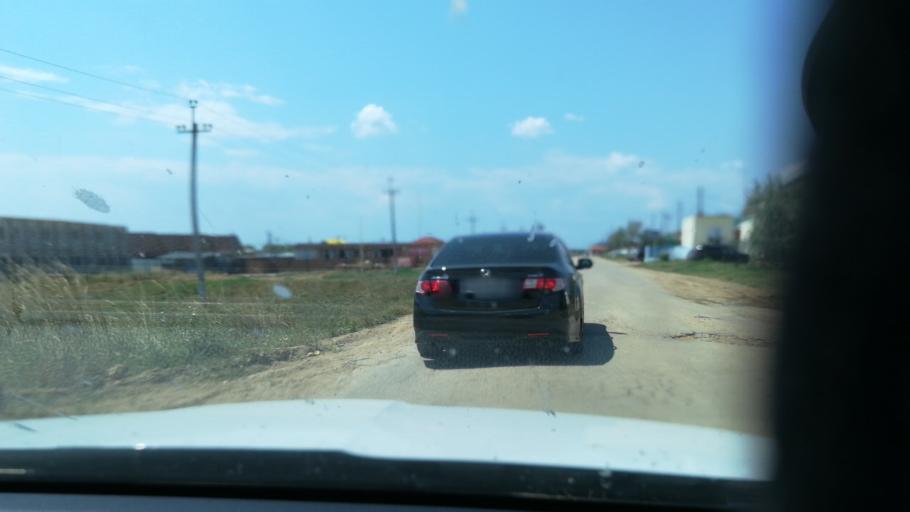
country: RU
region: Krasnodarskiy
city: Vyshestebliyevskaya
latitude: 45.1135
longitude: 36.8838
